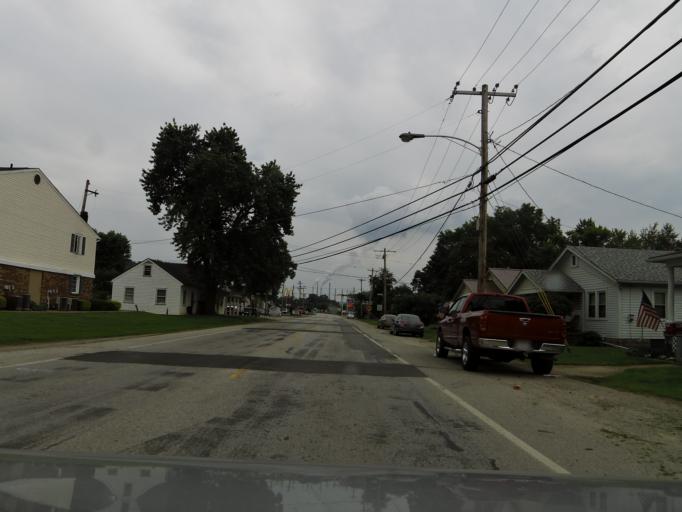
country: US
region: Ohio
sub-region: Brown County
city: Ripley
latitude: 38.7336
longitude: -83.8381
